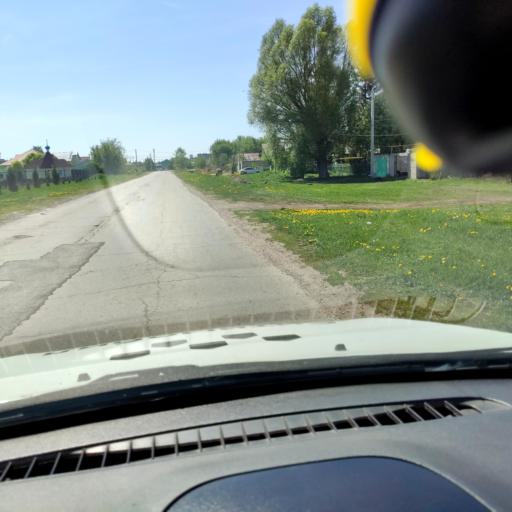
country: RU
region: Samara
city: Tol'yatti
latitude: 53.5725
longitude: 49.3143
